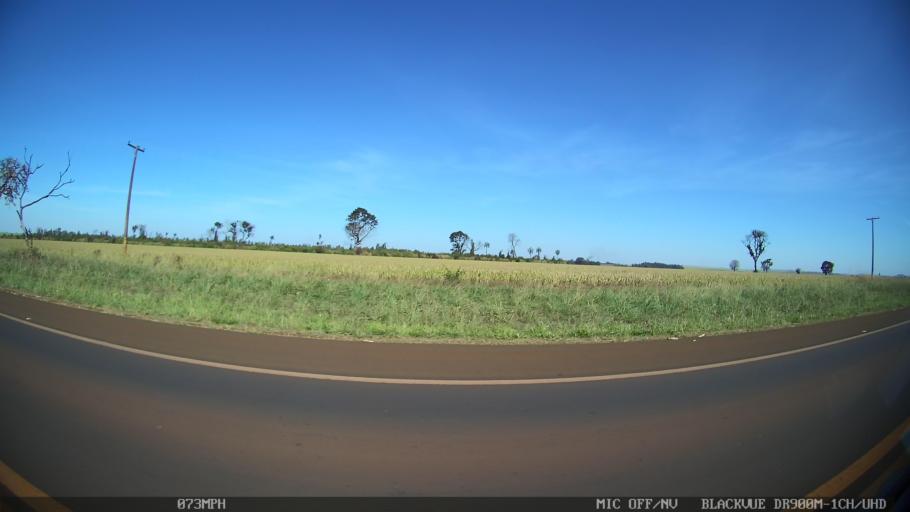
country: BR
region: Sao Paulo
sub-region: Guaira
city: Guaira
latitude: -20.4454
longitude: -48.3964
